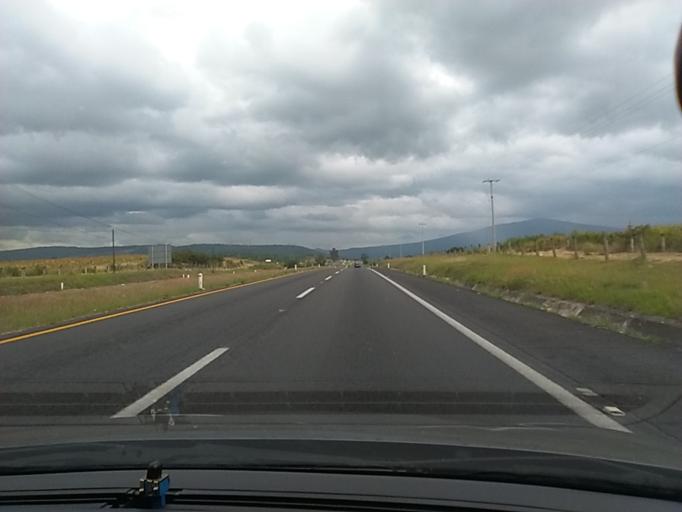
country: MX
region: Jalisco
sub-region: Zapotlanejo
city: La Mezquitera
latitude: 20.5976
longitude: -103.1140
